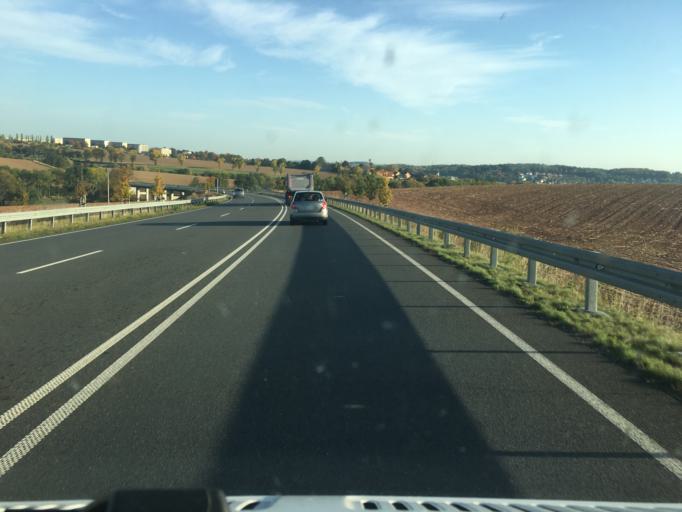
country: DE
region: Saxony
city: Neukirchen
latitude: 50.7977
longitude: 12.3724
